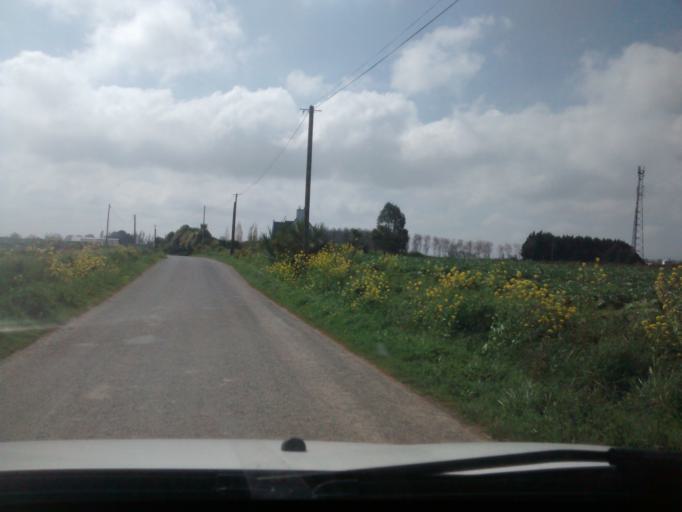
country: FR
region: Brittany
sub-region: Departement des Cotes-d'Armor
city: Penvenan
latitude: 48.8176
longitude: -3.3083
